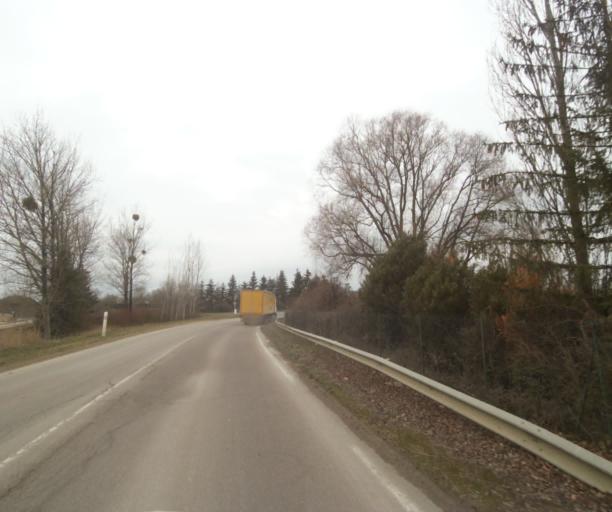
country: FR
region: Champagne-Ardenne
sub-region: Departement de la Haute-Marne
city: Villiers-en-Lieu
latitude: 48.6450
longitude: 4.9069
